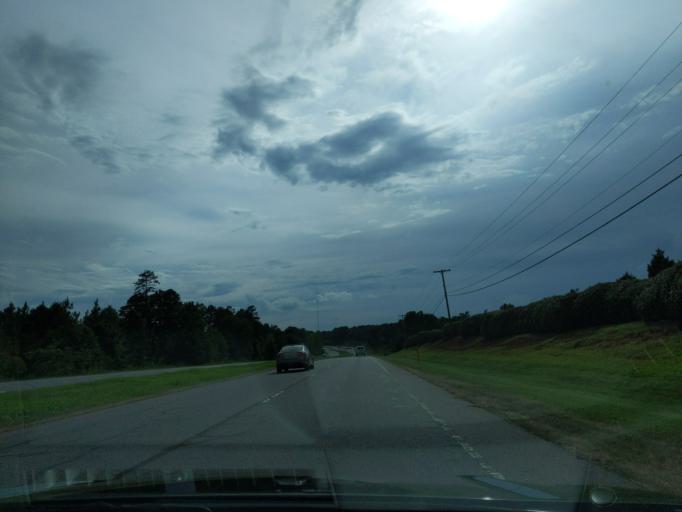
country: US
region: North Carolina
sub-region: Cabarrus County
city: Concord
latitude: 35.3693
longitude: -80.5712
